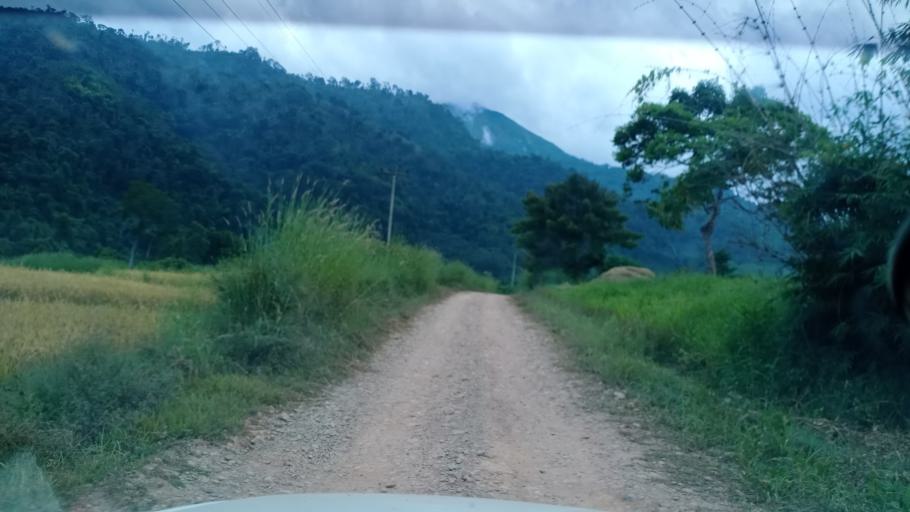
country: TH
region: Changwat Bueng Kan
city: Pak Khat
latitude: 18.7236
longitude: 103.2369
